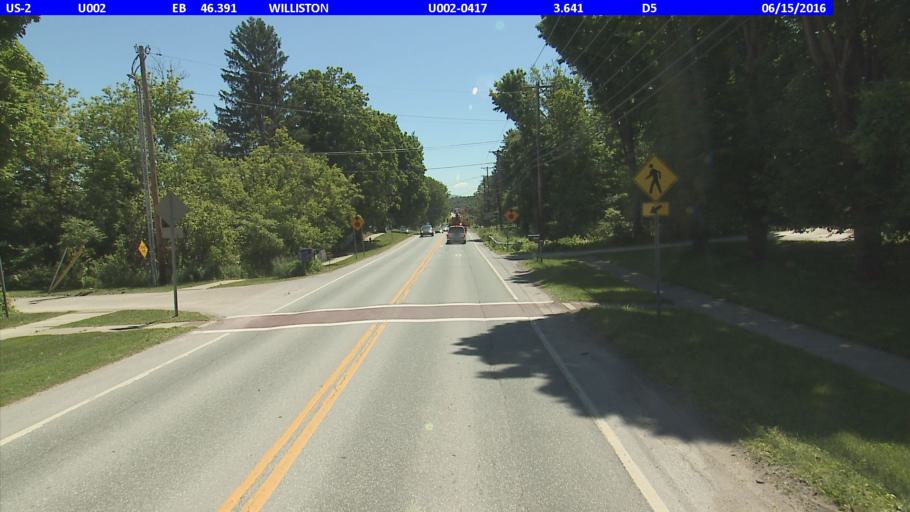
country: US
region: Vermont
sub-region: Chittenden County
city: Williston
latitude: 44.4379
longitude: -73.0701
